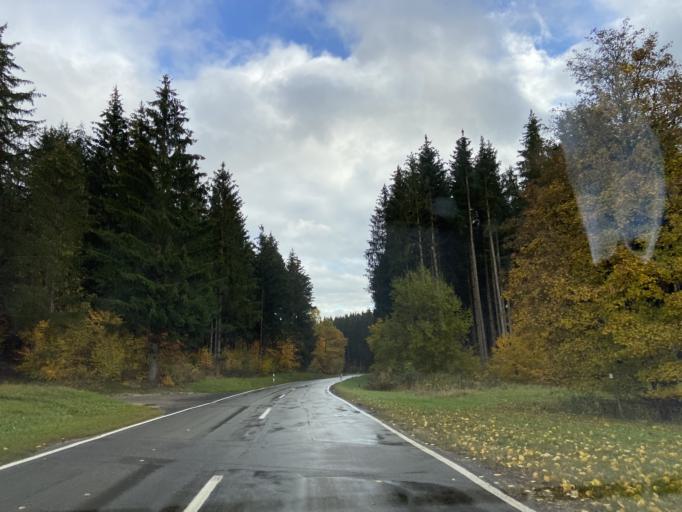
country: DE
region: Baden-Wuerttemberg
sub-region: Tuebingen Region
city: Schwenningen
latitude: 48.1003
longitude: 9.0114
